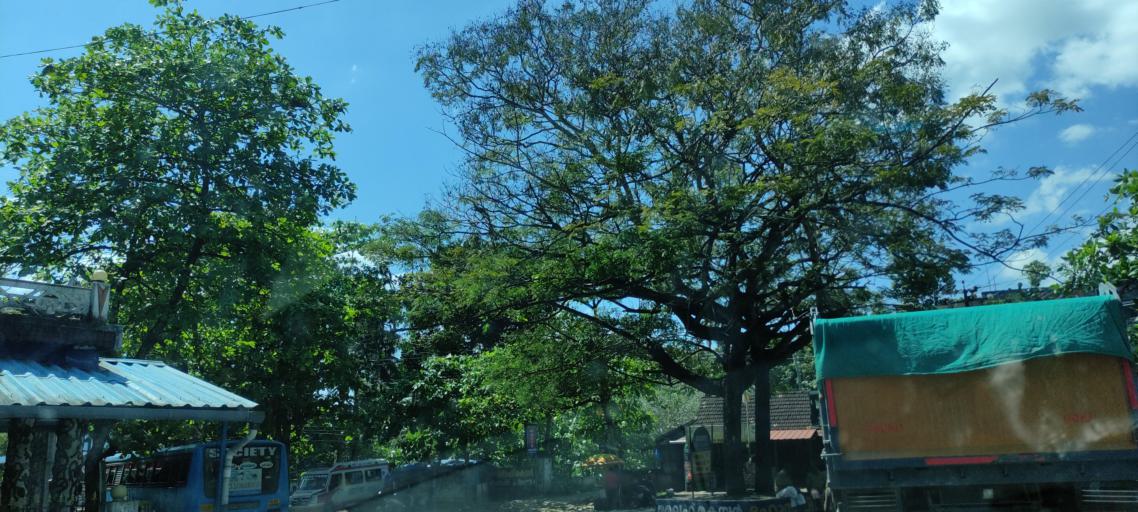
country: IN
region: Kerala
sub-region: Pattanamtitta
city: Adur
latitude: 9.1027
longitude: 76.6888
